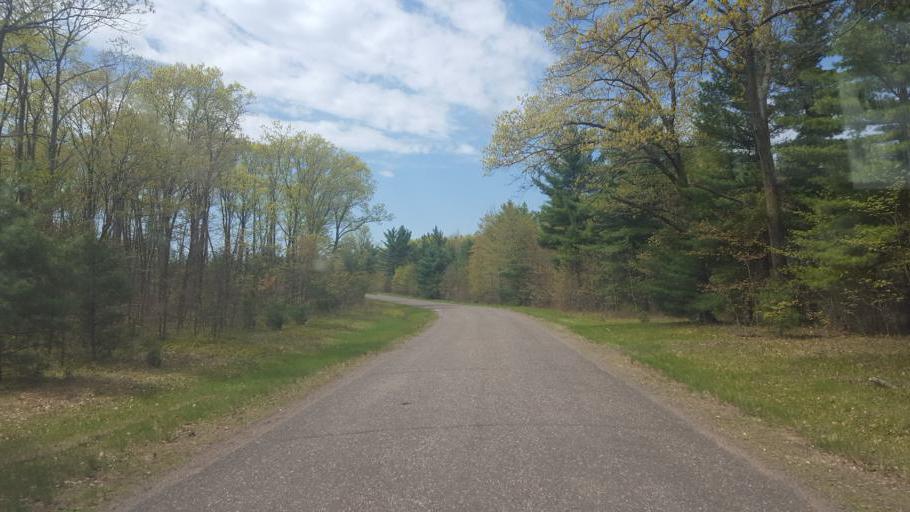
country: US
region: Wisconsin
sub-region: Clark County
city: Neillsville
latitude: 44.3532
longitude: -90.5090
